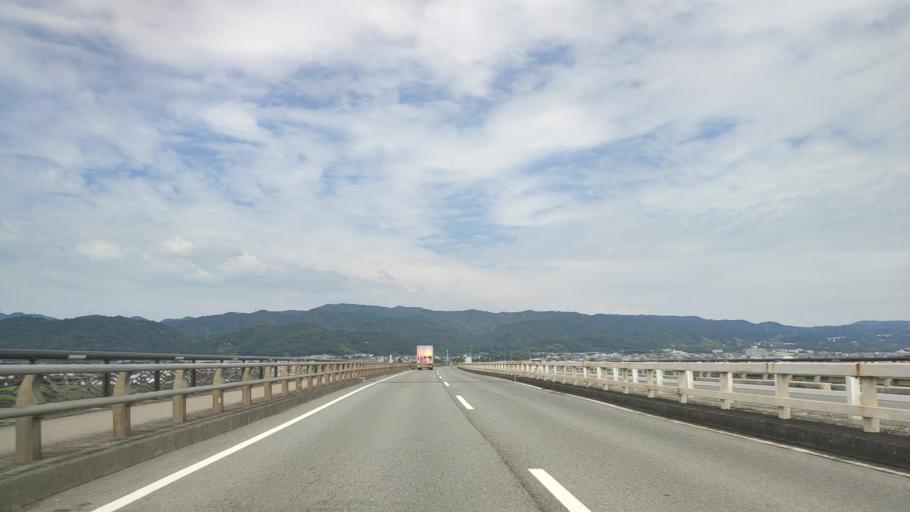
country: JP
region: Wakayama
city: Wakayama-shi
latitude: 34.2519
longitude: 135.2195
